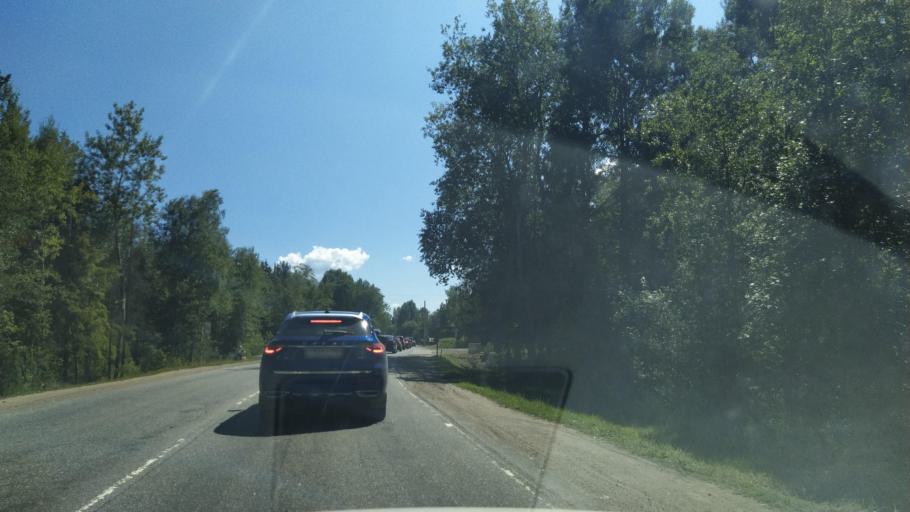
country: RU
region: Leningrad
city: Kirovsk
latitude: 59.9271
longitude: 30.9620
